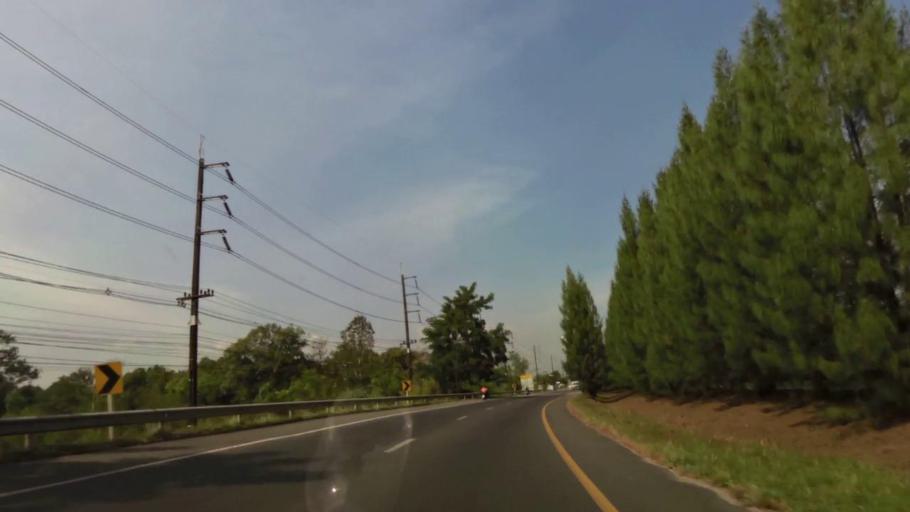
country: TH
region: Chanthaburi
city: Chanthaburi
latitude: 12.6434
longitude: 102.1307
